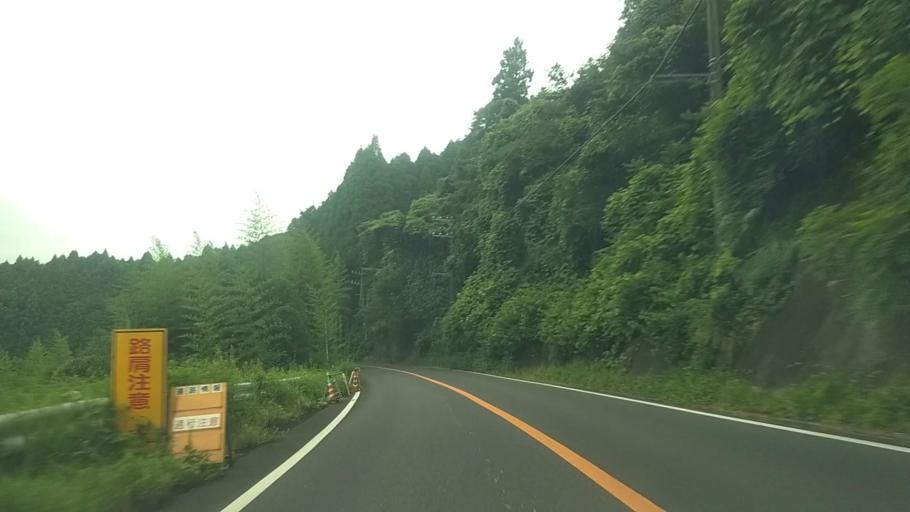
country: JP
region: Chiba
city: Kawaguchi
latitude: 35.2348
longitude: 140.0729
